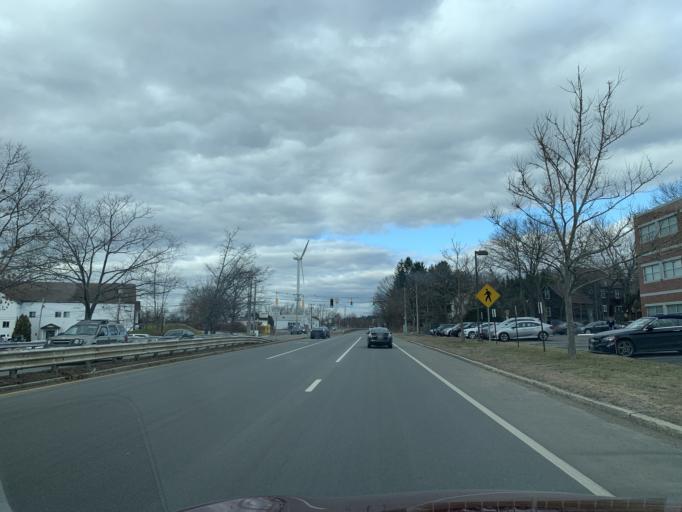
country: US
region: Massachusetts
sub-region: Essex County
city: Newburyport
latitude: 42.8000
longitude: -70.8767
